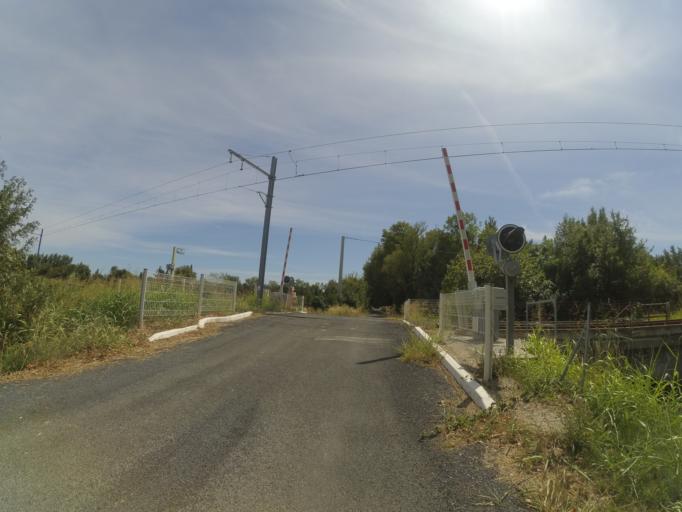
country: FR
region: Languedoc-Roussillon
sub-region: Departement des Pyrenees-Orientales
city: Ille-sur-Tet
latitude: 42.6785
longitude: 2.6465
